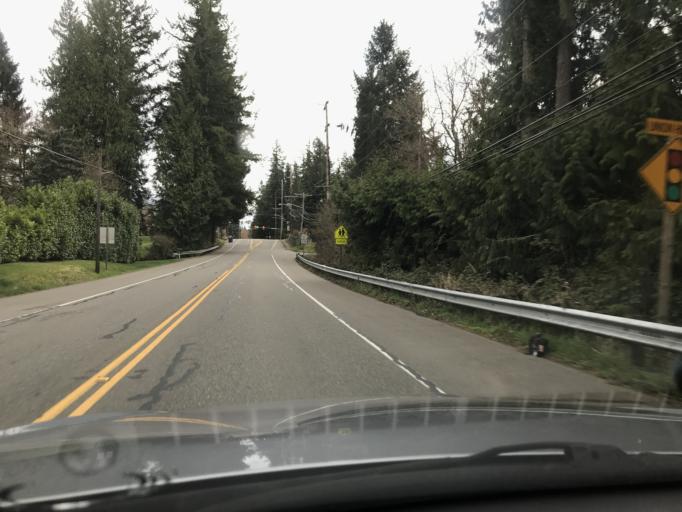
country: US
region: Washington
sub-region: King County
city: Union Hill-Novelty Hill
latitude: 47.6734
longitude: -122.0629
